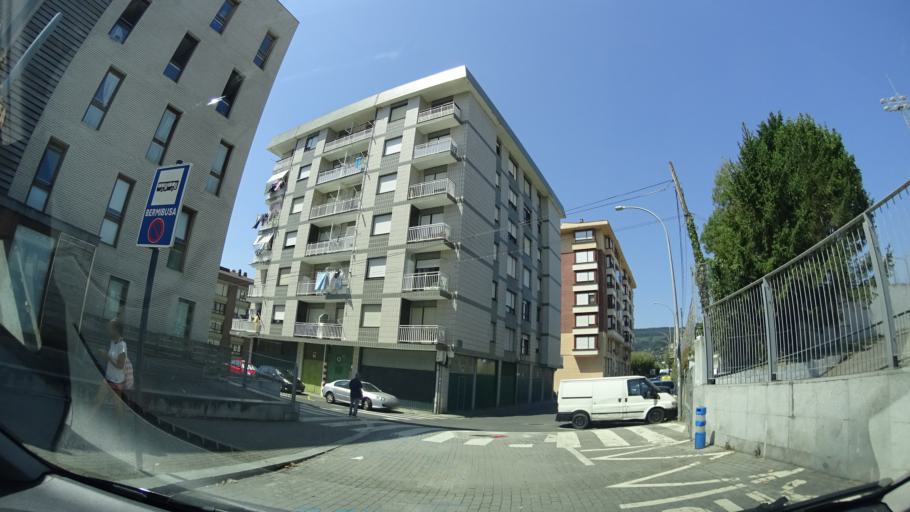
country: ES
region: Basque Country
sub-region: Bizkaia
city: Bermeo
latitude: 43.4224
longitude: -2.7242
